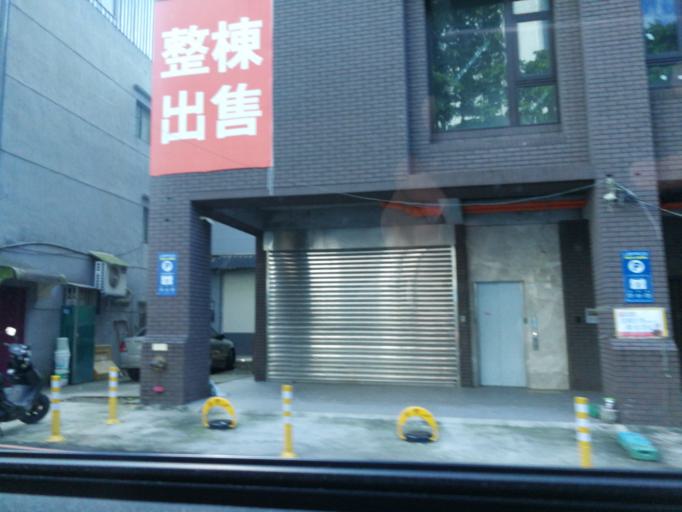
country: TW
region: Taipei
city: Taipei
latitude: 24.9539
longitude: 121.5569
